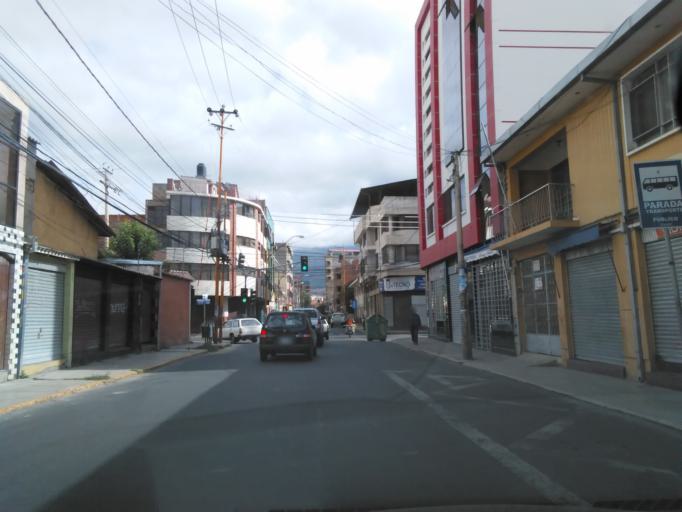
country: BO
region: Cochabamba
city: Cochabamba
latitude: -17.3896
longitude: -66.1527
